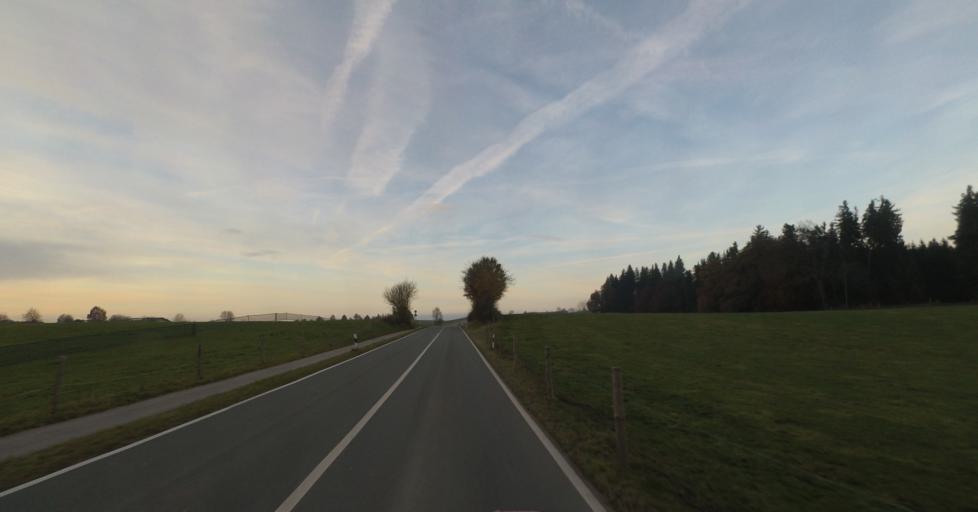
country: DE
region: Bavaria
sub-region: Upper Bavaria
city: Gstadt am Chiemsee
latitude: 47.8973
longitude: 12.3933
